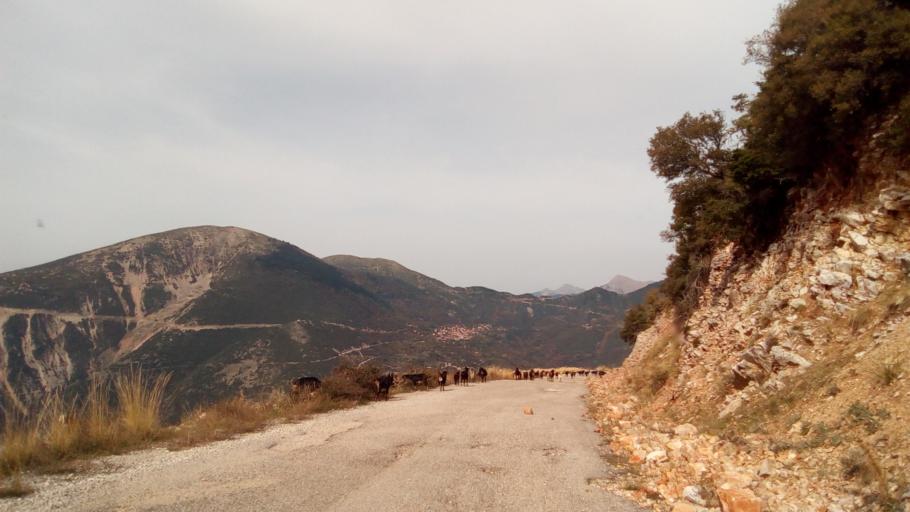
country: GR
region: West Greece
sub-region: Nomos Aitolias kai Akarnanias
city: Thermo
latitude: 38.5677
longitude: 21.8167
